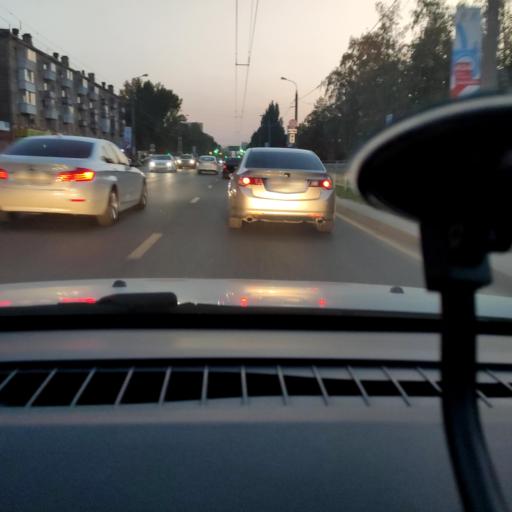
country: RU
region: Samara
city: Samara
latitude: 53.2316
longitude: 50.2130
